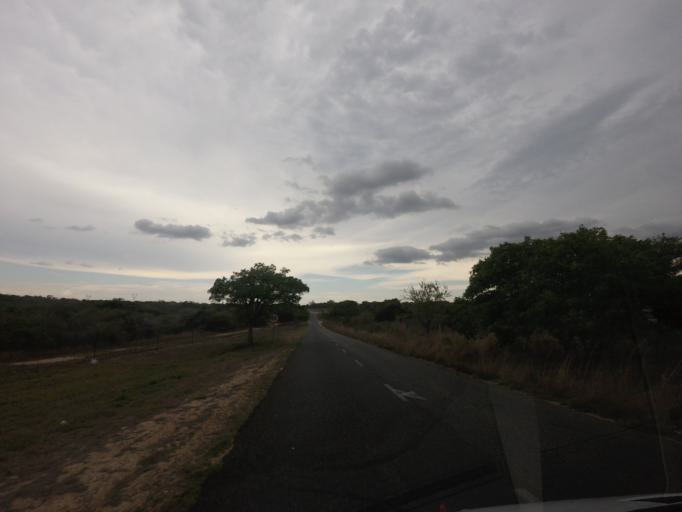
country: ZA
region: Limpopo
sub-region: Mopani District Municipality
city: Hoedspruit
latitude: -24.5394
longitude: 31.0220
